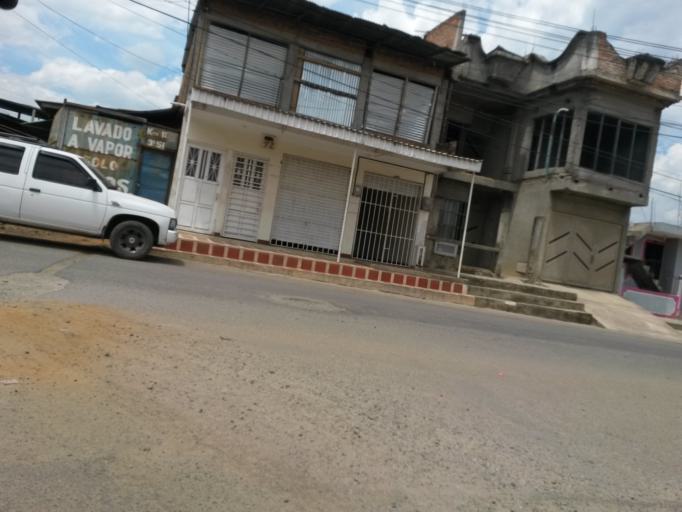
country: CO
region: Cauca
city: Santander de Quilichao
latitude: 3.0115
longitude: -76.4896
